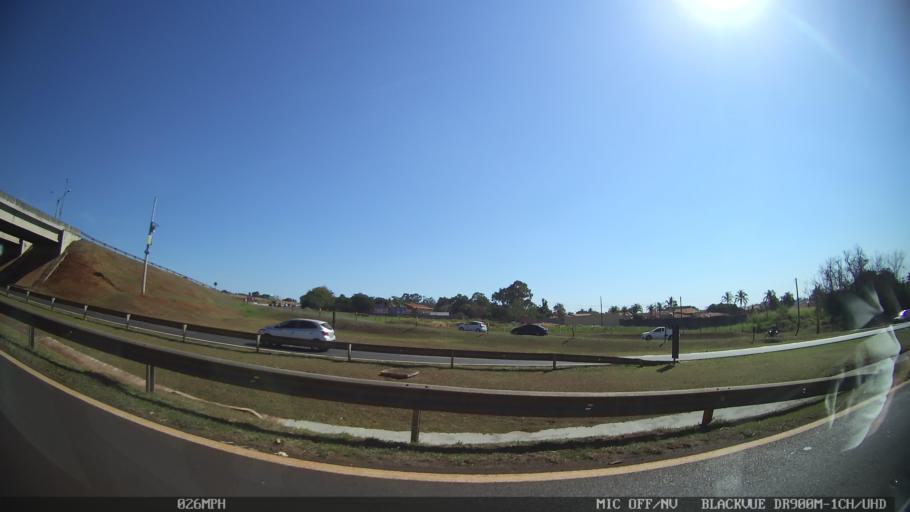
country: BR
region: Sao Paulo
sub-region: Ribeirao Preto
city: Ribeirao Preto
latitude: -21.2221
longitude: -47.7760
